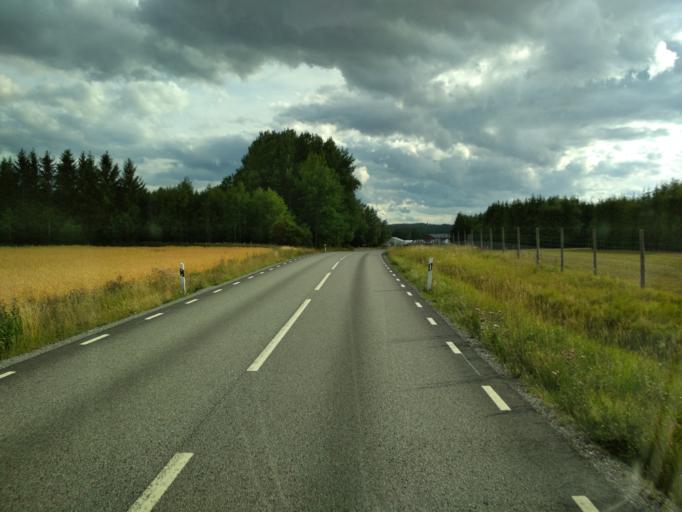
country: SE
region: Uppsala
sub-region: Habo Kommun
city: Balsta
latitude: 59.6379
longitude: 17.5237
